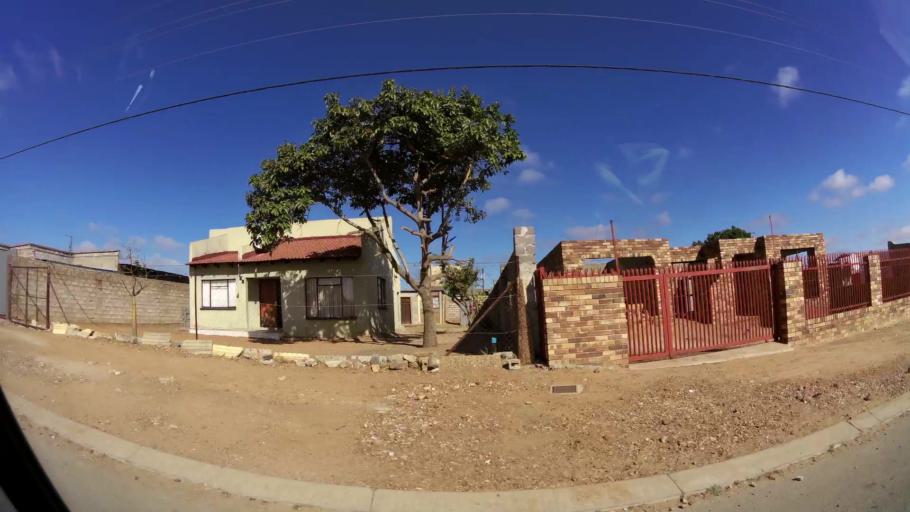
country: ZA
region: Limpopo
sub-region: Capricorn District Municipality
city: Polokwane
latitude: -23.8568
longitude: 29.3631
